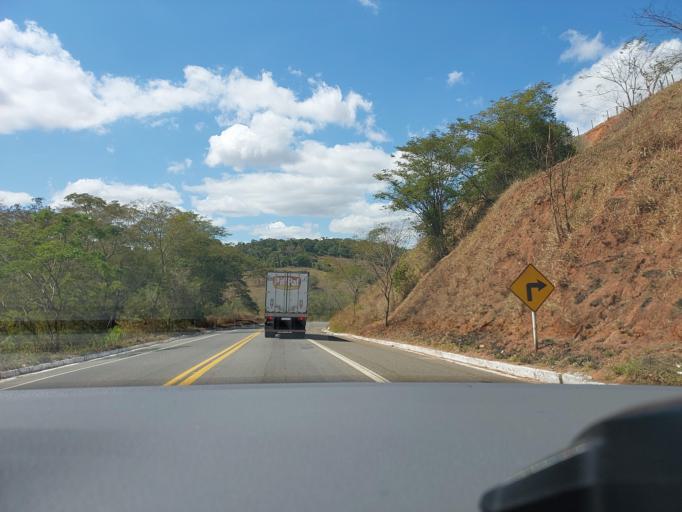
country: BR
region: Minas Gerais
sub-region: Muriae
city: Muriae
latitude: -21.1217
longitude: -42.2136
